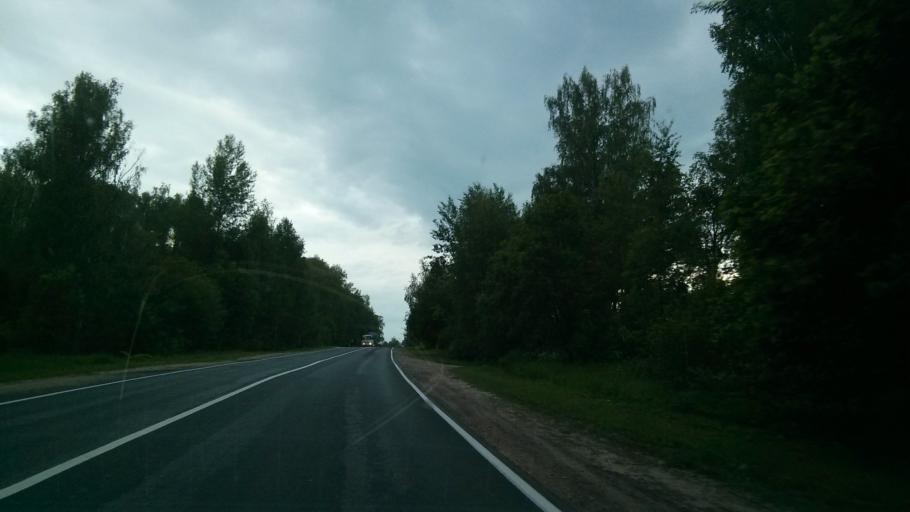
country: RU
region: Nizjnij Novgorod
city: Vacha
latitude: 55.7614
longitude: 42.5291
